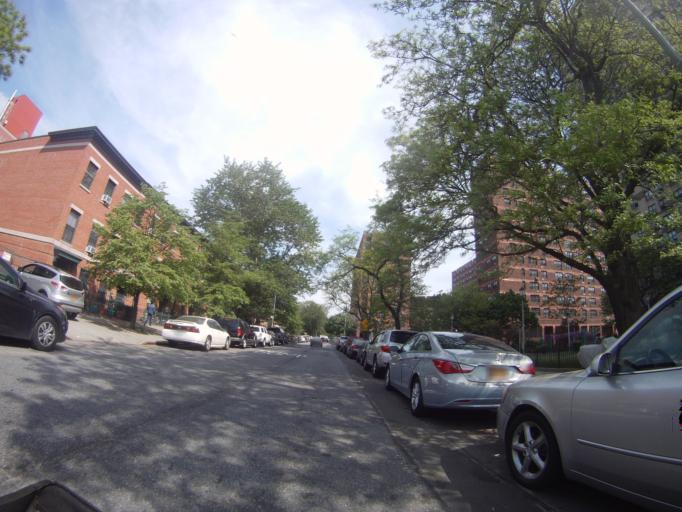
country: US
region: New York
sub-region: Kings County
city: Brooklyn
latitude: 40.6831
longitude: -73.9708
